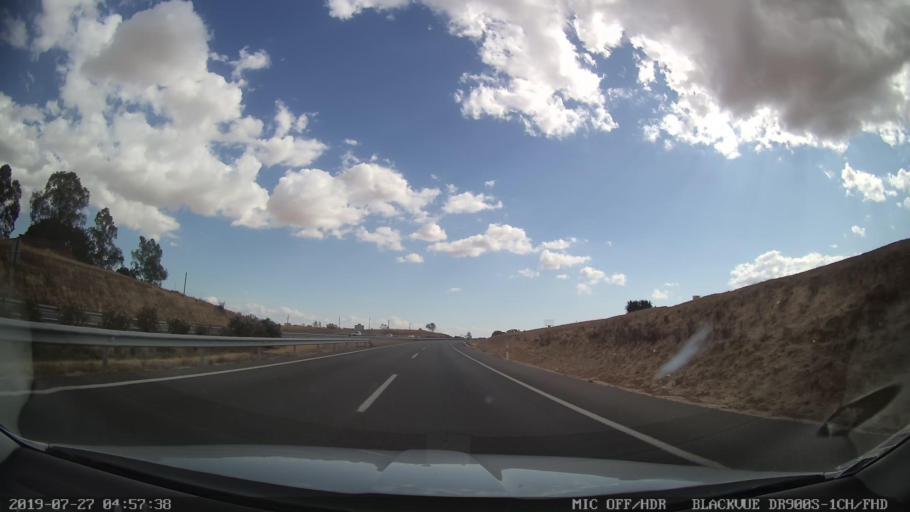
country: ES
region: Castille-La Mancha
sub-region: Province of Toledo
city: Valmojado
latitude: 40.2246
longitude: -4.0737
